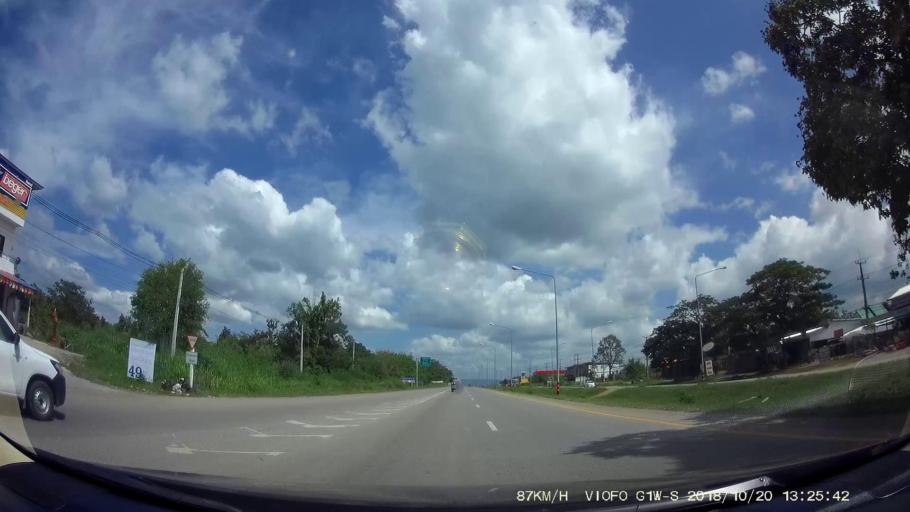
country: TH
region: Chaiyaphum
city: Khon San
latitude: 16.5946
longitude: 101.9358
